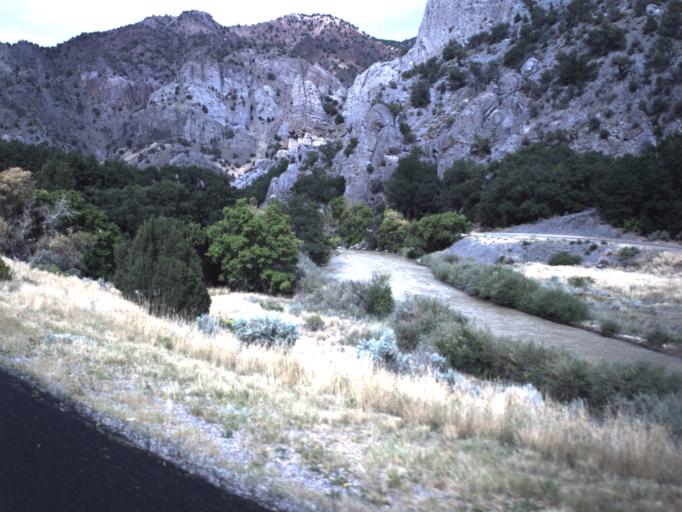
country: US
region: Utah
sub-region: Sevier County
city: Monroe
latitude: 38.5328
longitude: -112.2708
